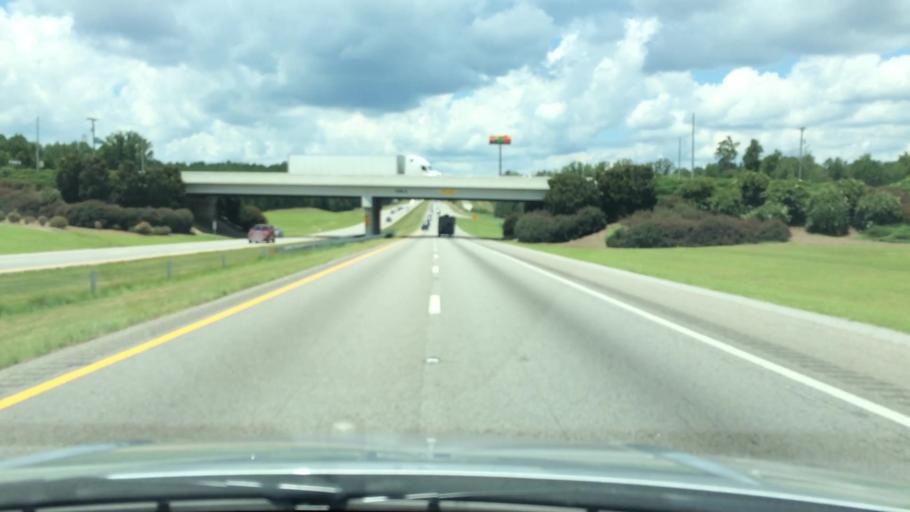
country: US
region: South Carolina
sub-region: Newberry County
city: Newberry
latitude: 34.2927
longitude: -81.5450
